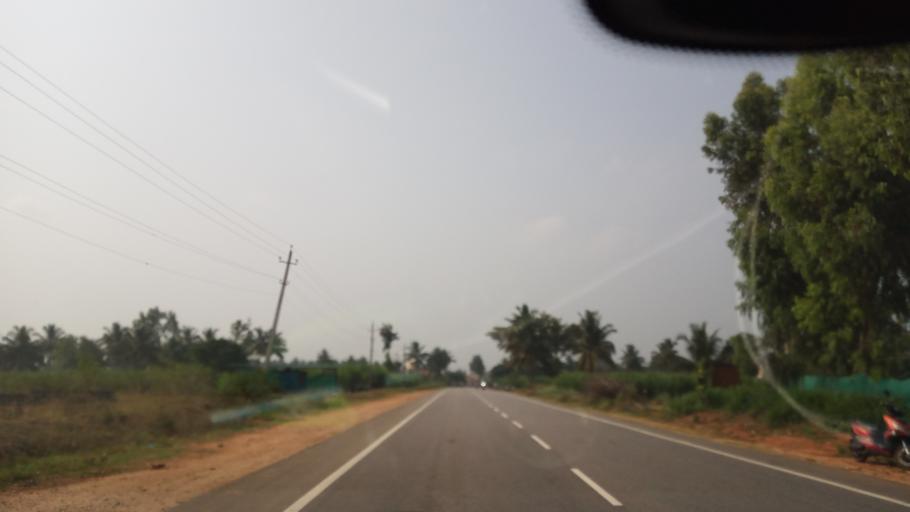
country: IN
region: Karnataka
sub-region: Mandya
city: Pandavapura
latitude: 12.5566
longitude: 76.6712
